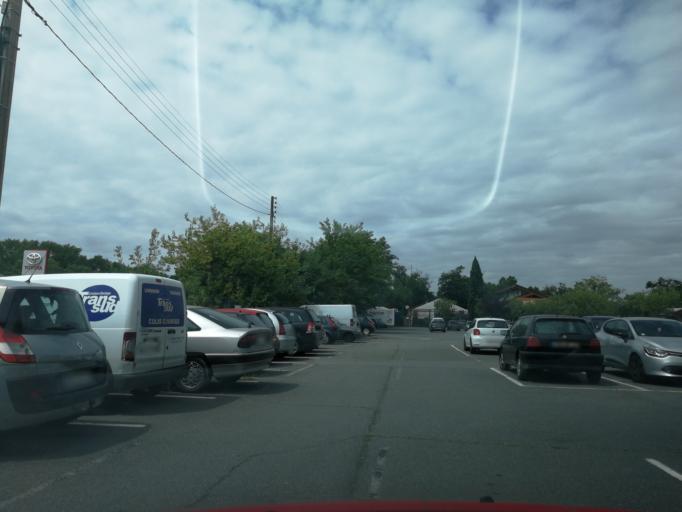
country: FR
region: Midi-Pyrenees
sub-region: Departement de la Haute-Garonne
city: Ramonville-Saint-Agne
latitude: 43.5685
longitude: 1.4993
